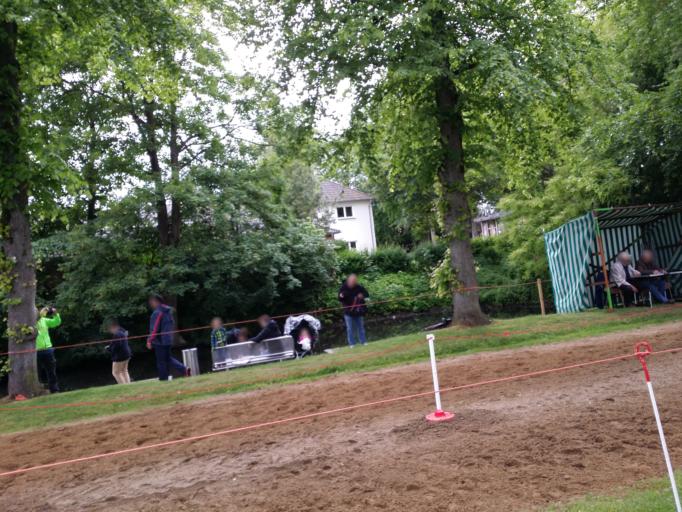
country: DE
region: Schleswig-Holstein
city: Tonning
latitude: 54.3152
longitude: 8.9427
